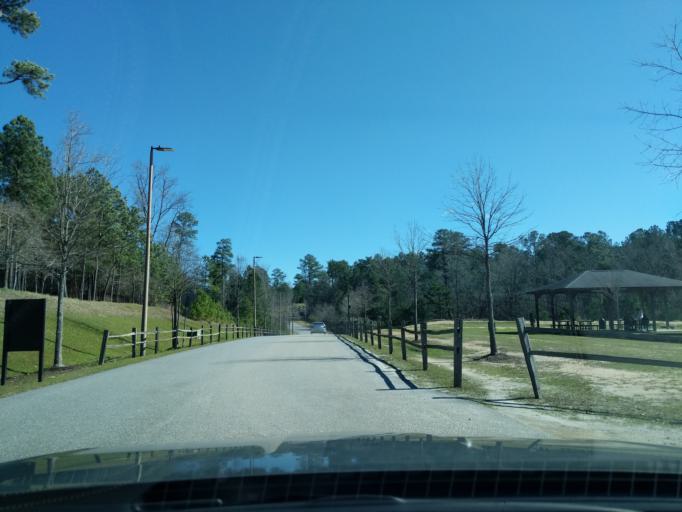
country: US
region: Georgia
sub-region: Columbia County
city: Evans
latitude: 33.5545
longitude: -82.1719
